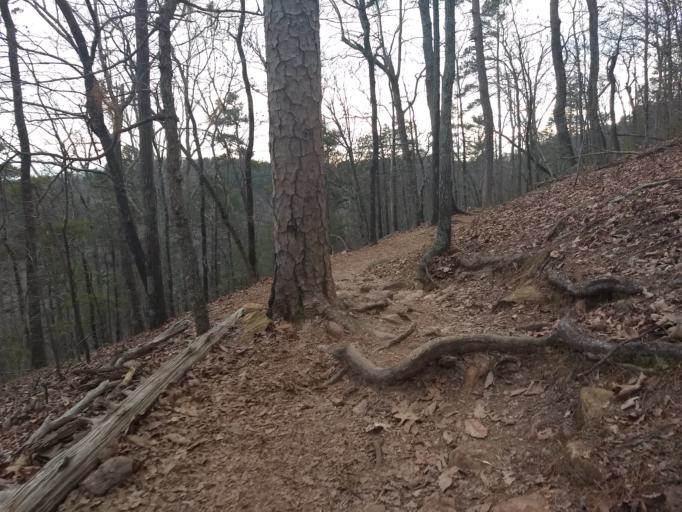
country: US
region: South Carolina
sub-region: Greenville County
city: Travelers Rest
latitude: 34.9474
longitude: -82.3871
